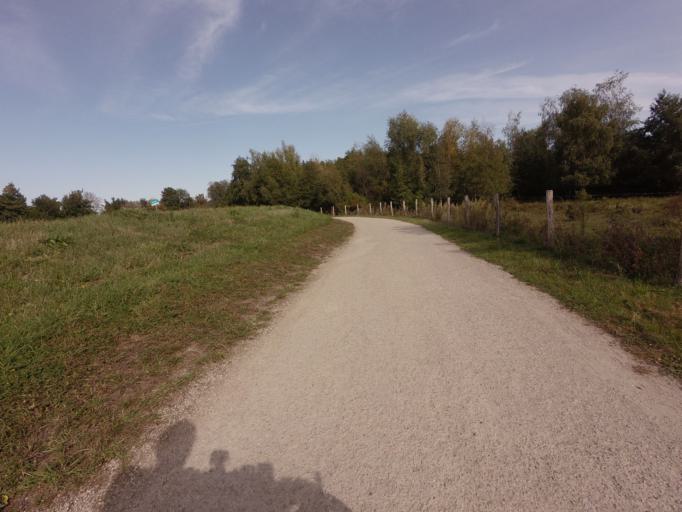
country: NL
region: Limburg
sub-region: Gemeente Maasgouw
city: Maasbracht
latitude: 51.1569
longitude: 5.8656
